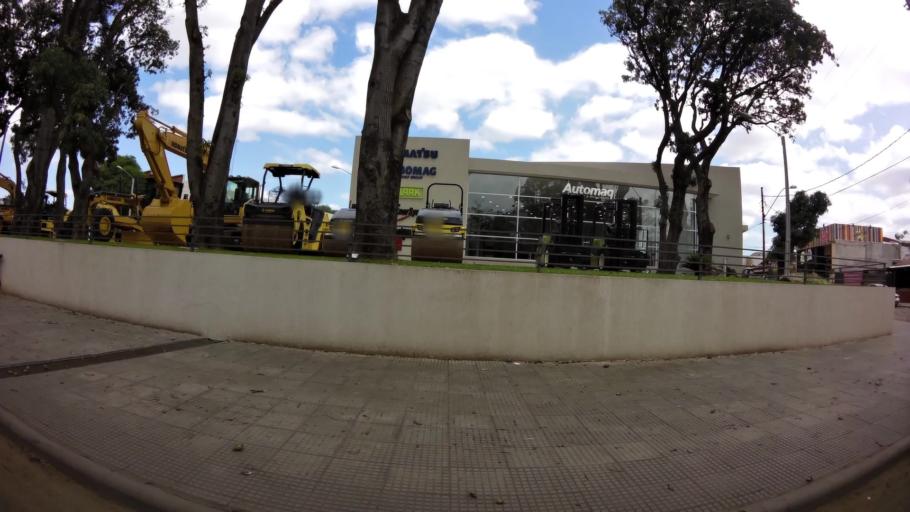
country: PY
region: Central
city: Fernando de la Mora
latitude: -25.3045
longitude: -57.5391
